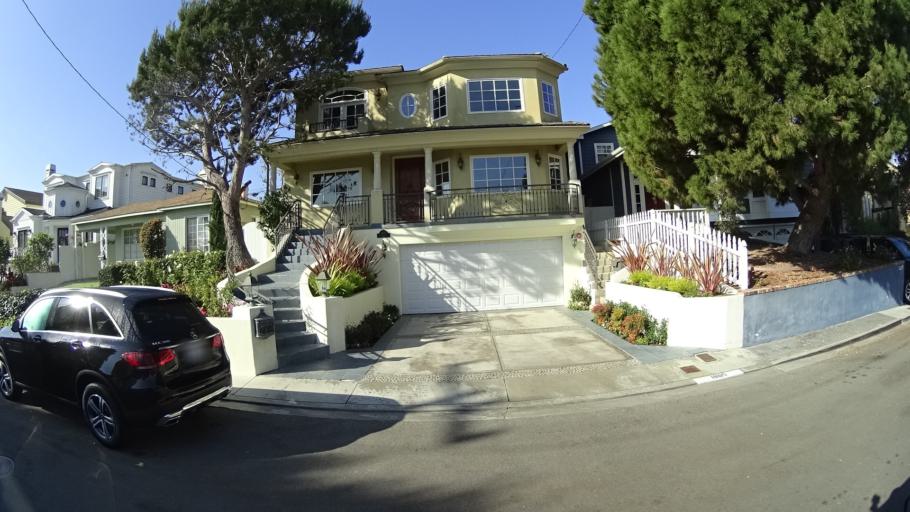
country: US
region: California
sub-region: Los Angeles County
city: Manhattan Beach
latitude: 33.8915
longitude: -118.3987
